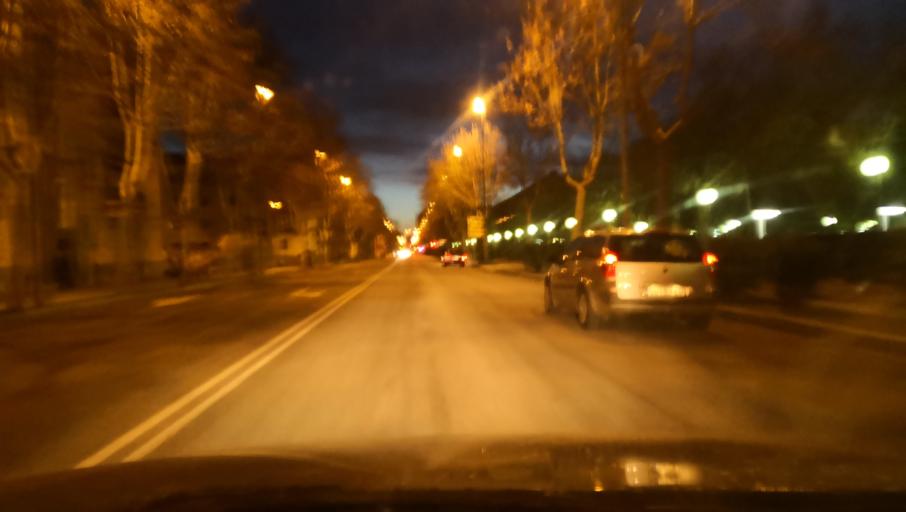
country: ES
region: Castille and Leon
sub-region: Provincia de Zamora
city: Zamora
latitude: 41.5130
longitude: -5.7327
